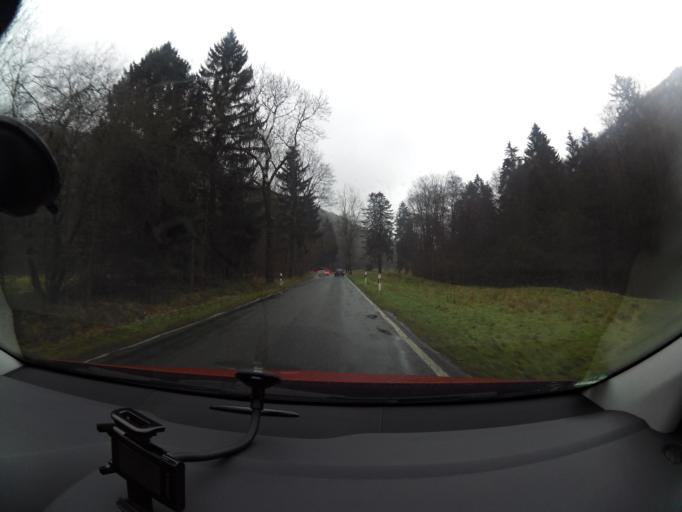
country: DE
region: Lower Saxony
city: Herzberg am Harz
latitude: 51.6787
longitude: 10.3760
